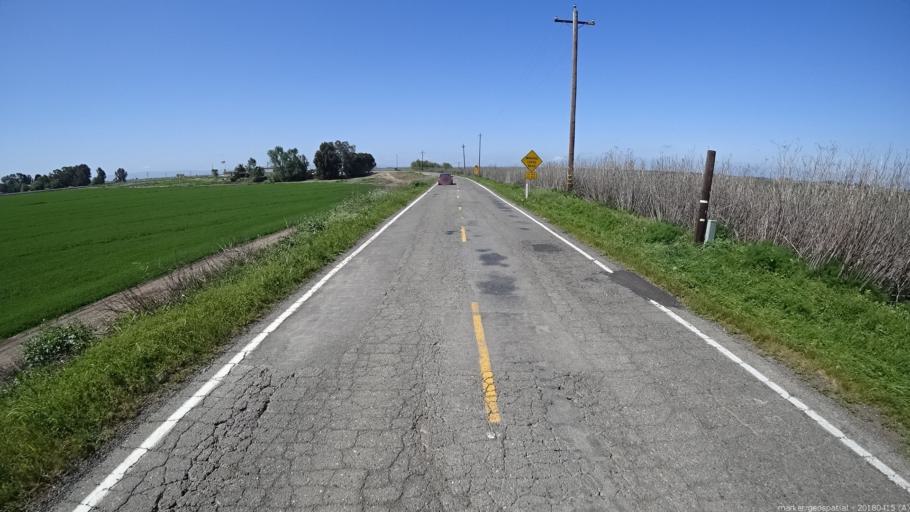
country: US
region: California
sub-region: Solano County
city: Rio Vista
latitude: 38.1445
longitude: -121.6220
